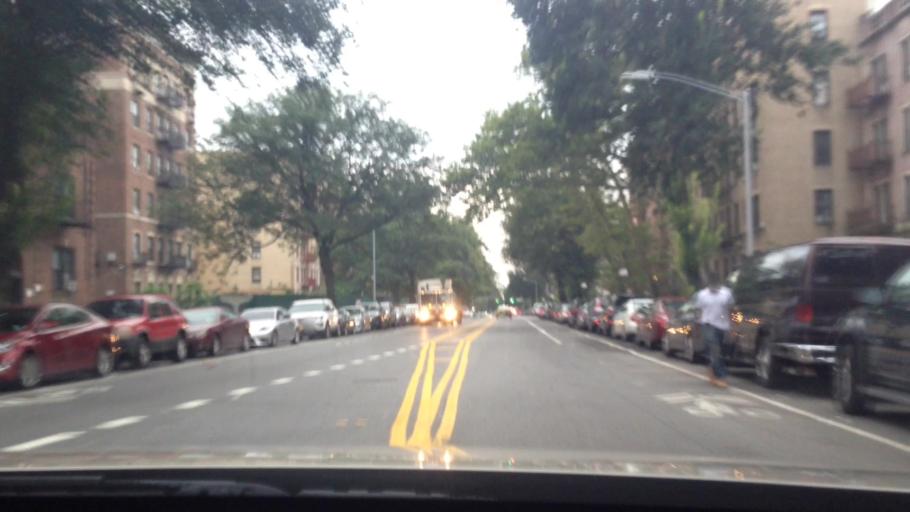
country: US
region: New York
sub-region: Kings County
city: Brooklyn
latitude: 40.6498
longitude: -73.9609
